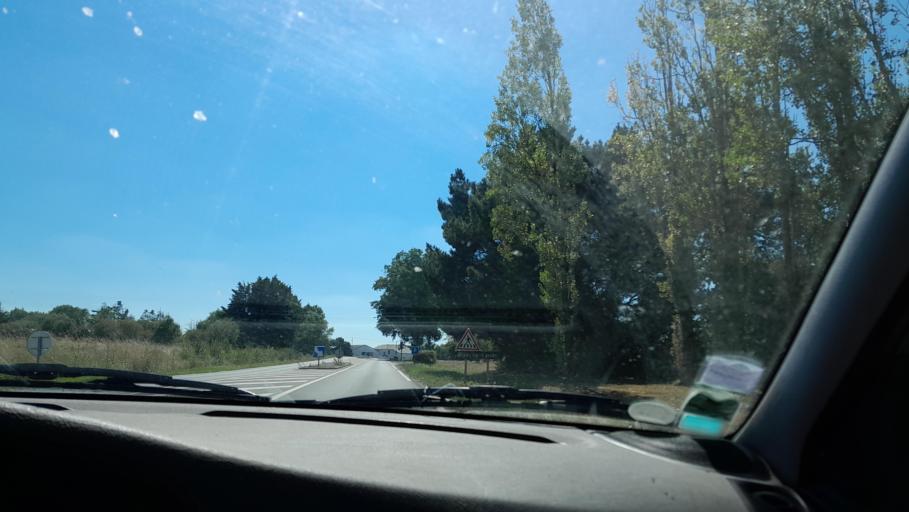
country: FR
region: Pays de la Loire
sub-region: Departement de Maine-et-Loire
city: Champtoceaux
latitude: 47.3552
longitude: -1.2520
